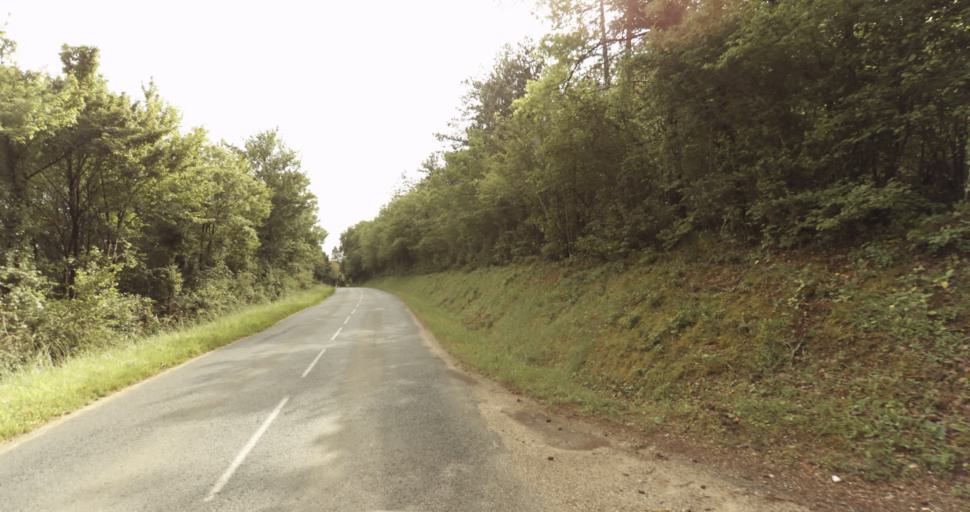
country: FR
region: Aquitaine
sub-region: Departement de la Dordogne
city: Vergt
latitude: 44.9388
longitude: 0.7892
